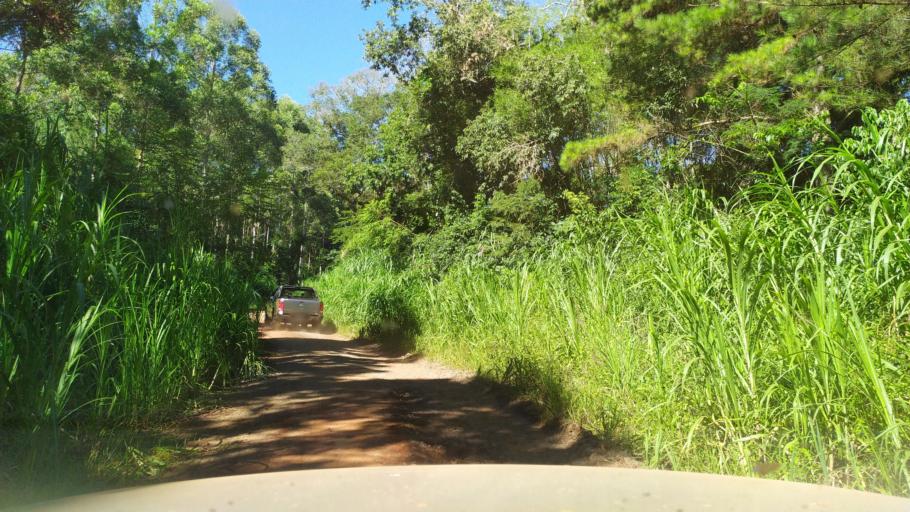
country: AR
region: Misiones
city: Caraguatay
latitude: -26.6757
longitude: -54.7010
